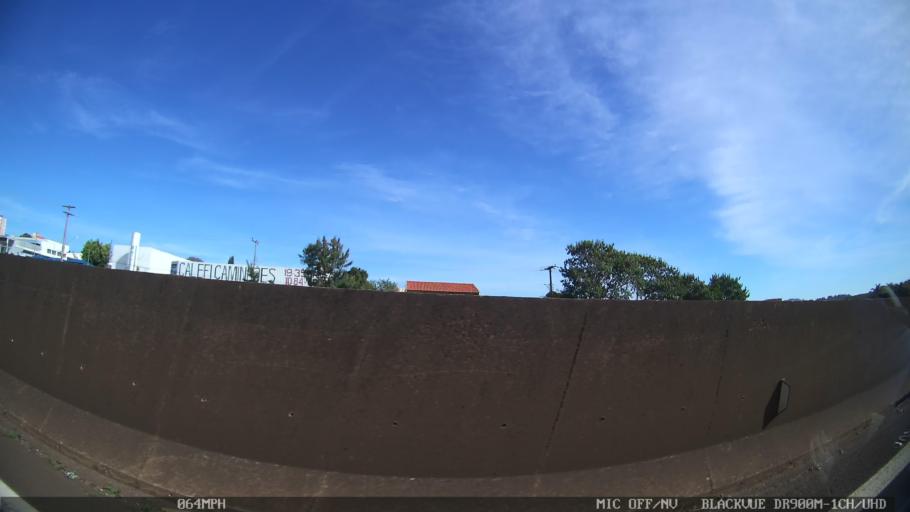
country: BR
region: Sao Paulo
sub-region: Araras
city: Araras
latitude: -22.3514
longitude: -47.3948
